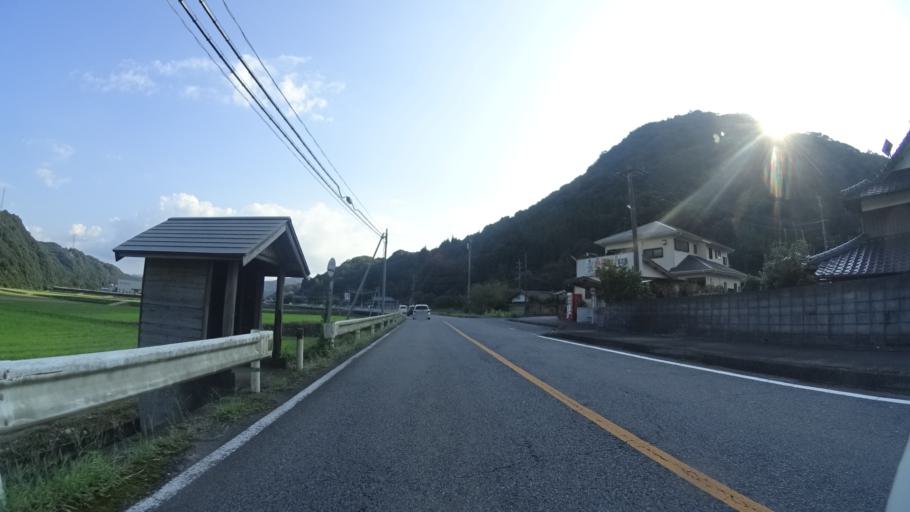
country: JP
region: Oita
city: Bungo-Takada-shi
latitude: 33.4728
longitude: 131.3284
